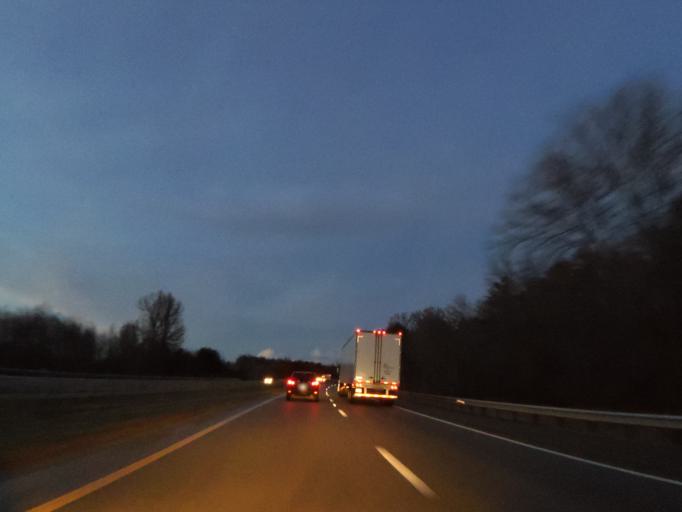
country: US
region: Kentucky
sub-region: Whitley County
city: Corbin
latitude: 36.8867
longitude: -84.1499
